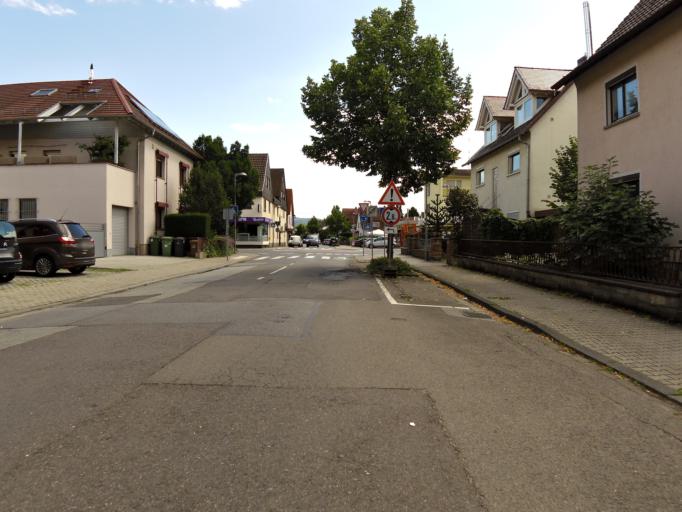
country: DE
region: Hesse
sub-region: Regierungsbezirk Darmstadt
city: Heppenheim an der Bergstrasse
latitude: 49.6397
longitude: 8.6304
